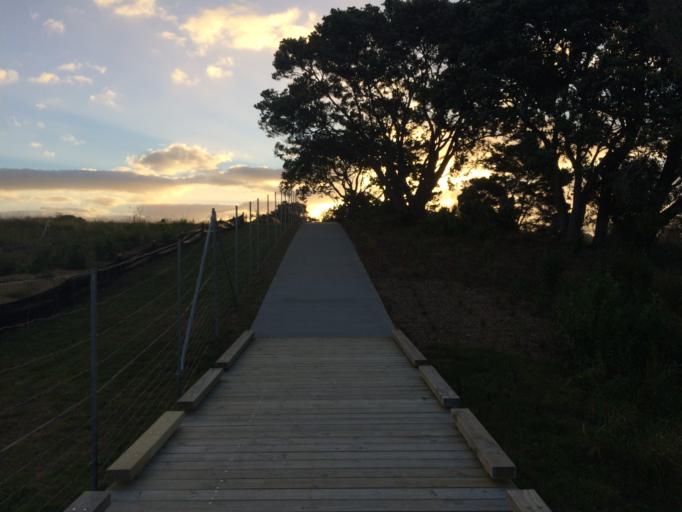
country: NZ
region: Auckland
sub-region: Auckland
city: Rosebank
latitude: -36.7876
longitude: 174.6624
